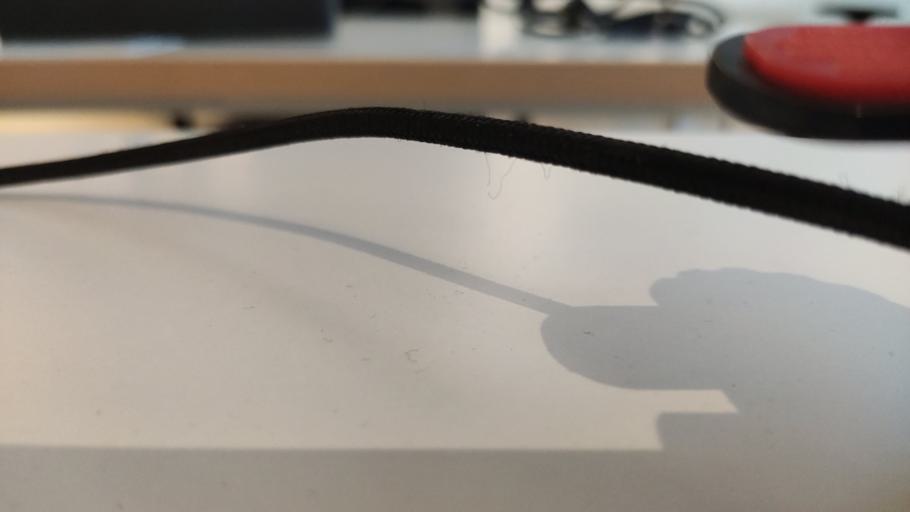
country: RU
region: Moskovskaya
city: Novopetrovskoye
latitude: 55.8974
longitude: 36.4317
